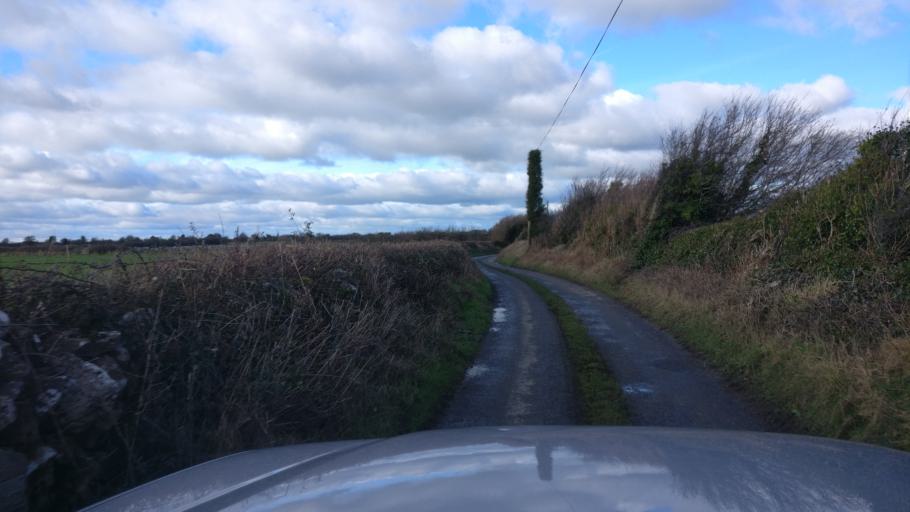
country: IE
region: Connaught
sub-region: County Galway
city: Athenry
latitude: 53.2307
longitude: -8.8002
